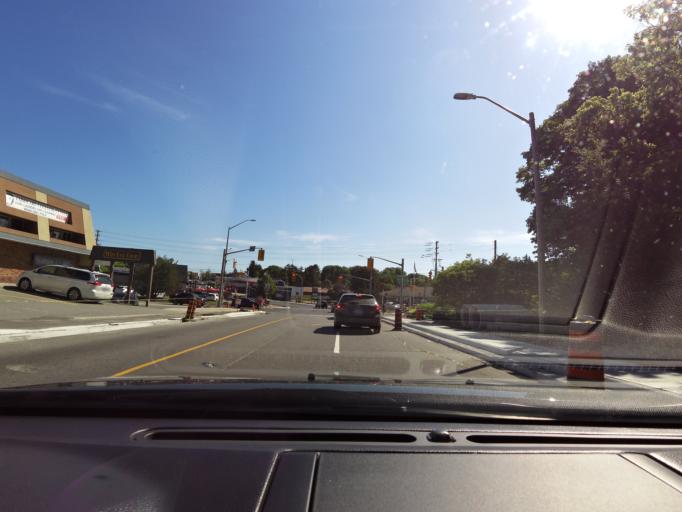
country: CA
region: Ontario
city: Huntsville
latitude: 45.3283
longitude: -79.2126
